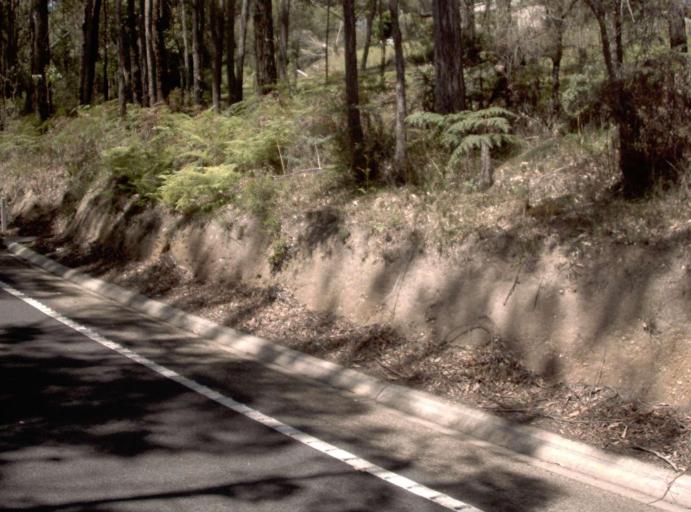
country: AU
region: Victoria
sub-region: East Gippsland
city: Lakes Entrance
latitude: -37.6951
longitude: 148.7235
